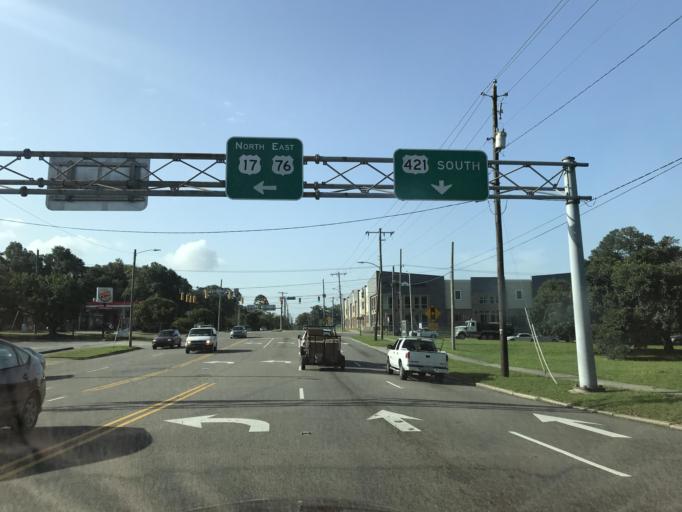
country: US
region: North Carolina
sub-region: New Hanover County
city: Wilmington
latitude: 34.2250
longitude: -77.9448
